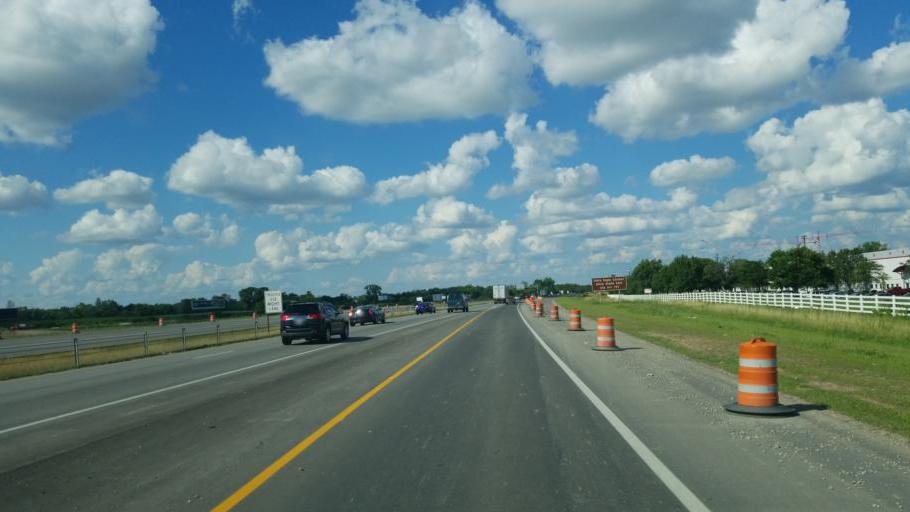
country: US
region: Ohio
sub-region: Franklin County
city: Grove City
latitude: 39.8464
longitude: -83.0855
